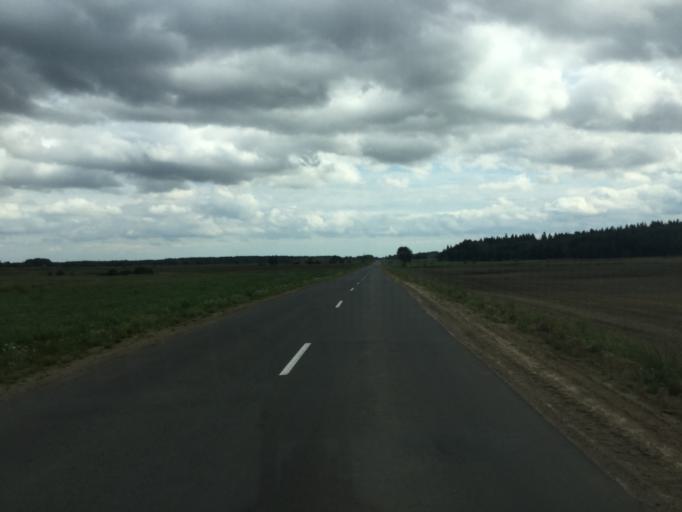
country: BY
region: Vitebsk
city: Vitebsk
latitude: 55.1425
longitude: 30.2885
